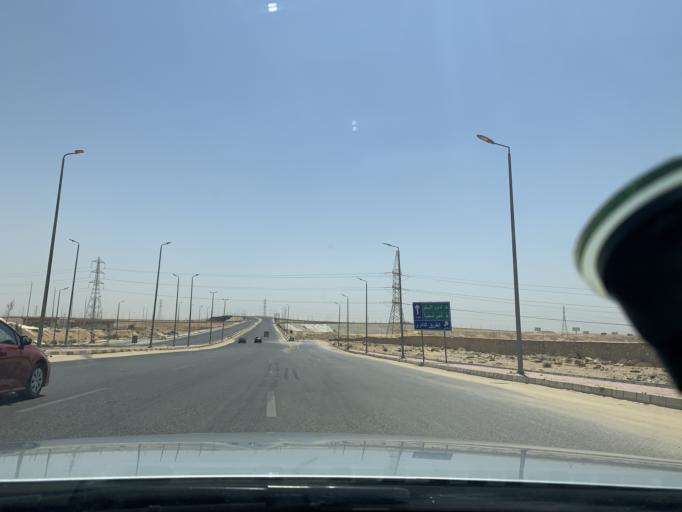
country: EG
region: Muhafazat al Qahirah
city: Halwan
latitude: 29.9747
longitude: 31.4702
